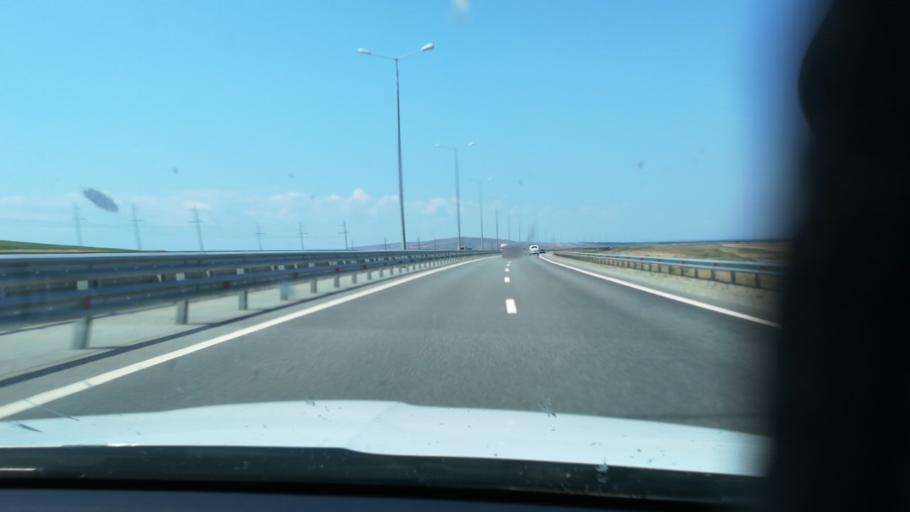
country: RU
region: Krasnodarskiy
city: Vyshestebliyevskaya
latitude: 45.2277
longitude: 36.9713
